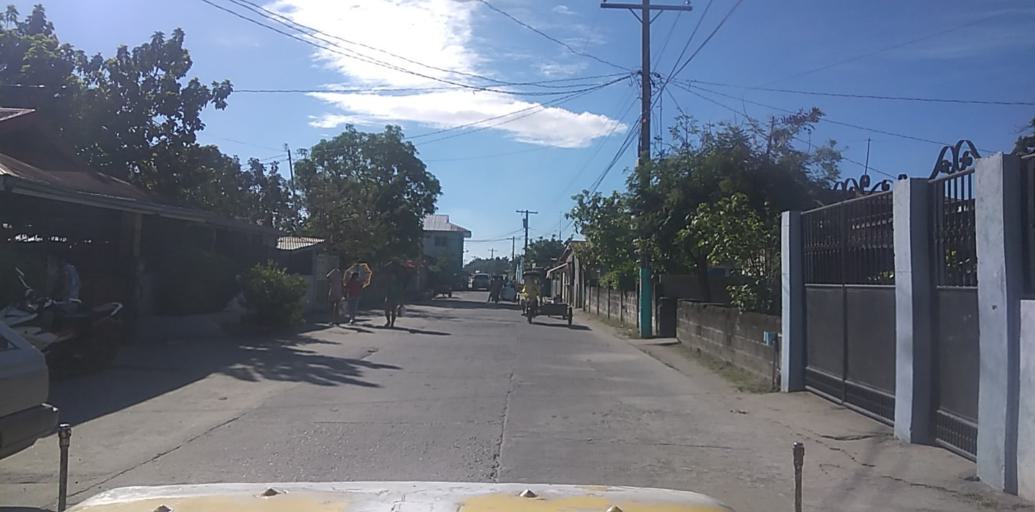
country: PH
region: Central Luzon
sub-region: Province of Pampanga
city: San Patricio
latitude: 15.1106
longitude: 120.7119
